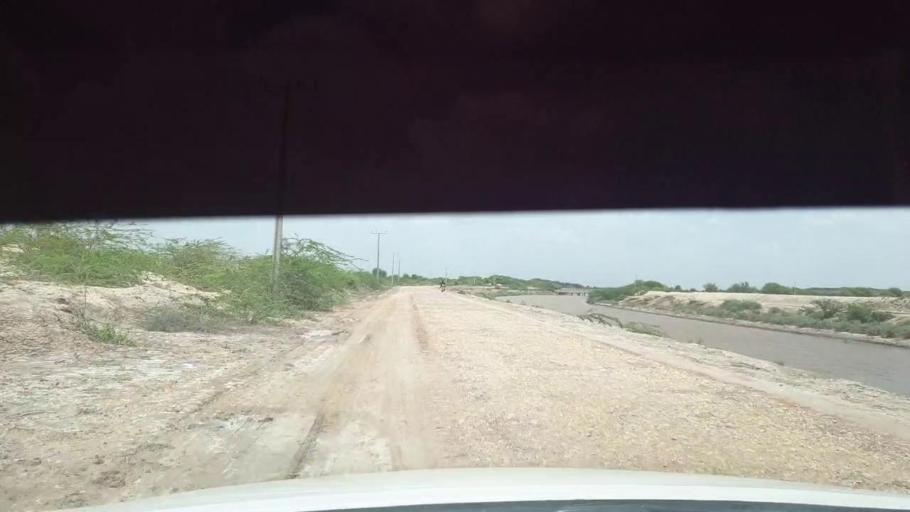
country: PK
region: Sindh
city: Kadhan
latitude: 24.5273
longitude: 69.1246
